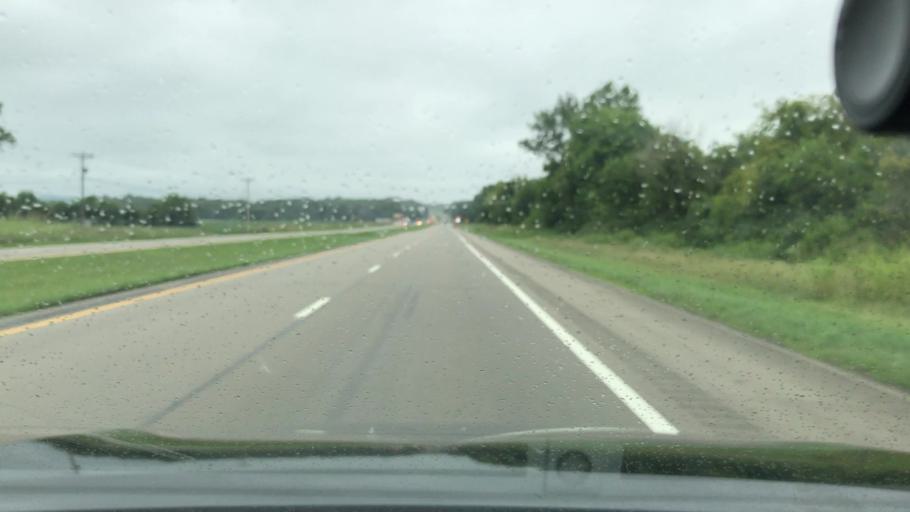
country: US
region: Ohio
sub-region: Ross County
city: Kingston
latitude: 39.4494
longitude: -82.9726
